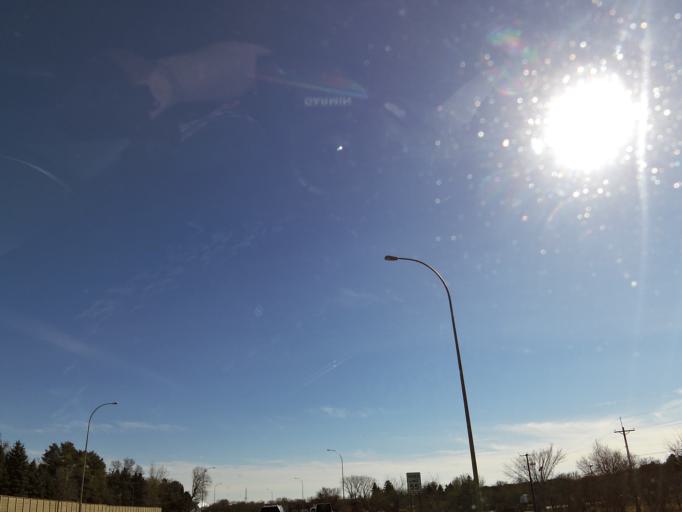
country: US
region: Minnesota
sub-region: Hennepin County
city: Edina
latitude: 44.8838
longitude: -93.3995
